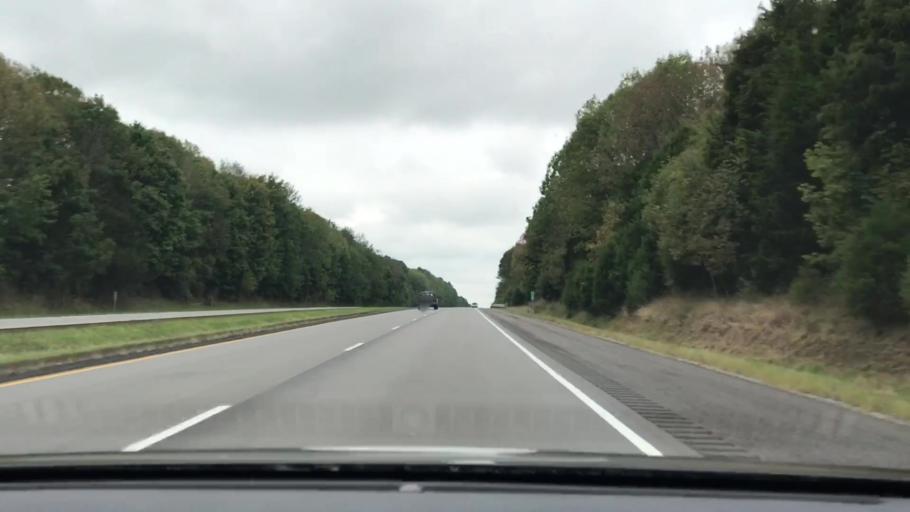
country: US
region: Kentucky
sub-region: Barren County
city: Glasgow
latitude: 36.9964
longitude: -85.8271
